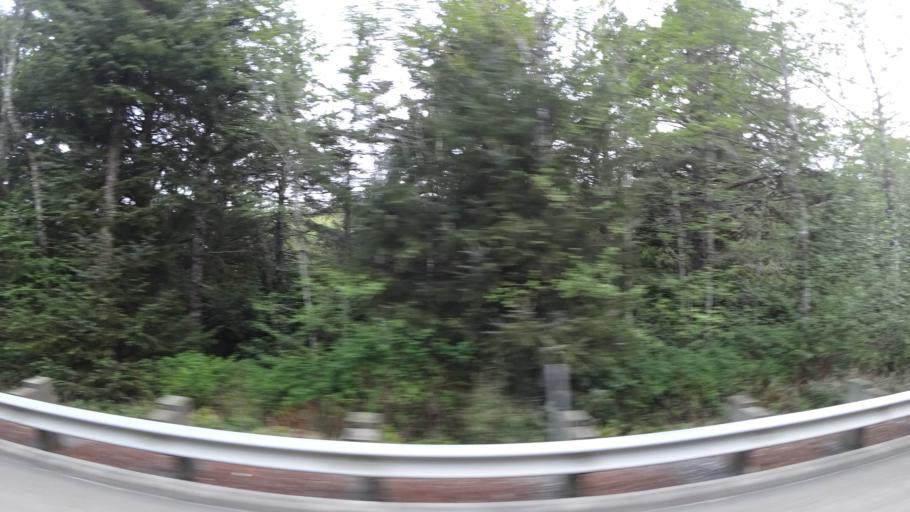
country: US
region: Oregon
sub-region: Coos County
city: Bandon
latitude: 43.1917
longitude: -124.3252
